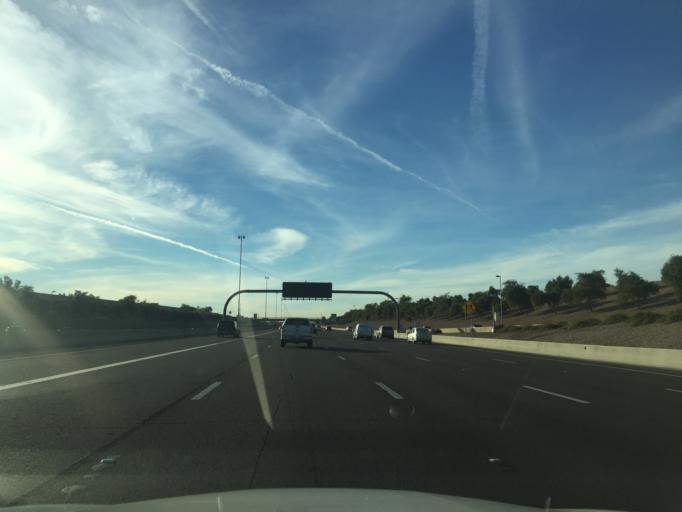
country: US
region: Arizona
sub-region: Maricopa County
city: Gilbert
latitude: 33.3864
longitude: -111.7901
